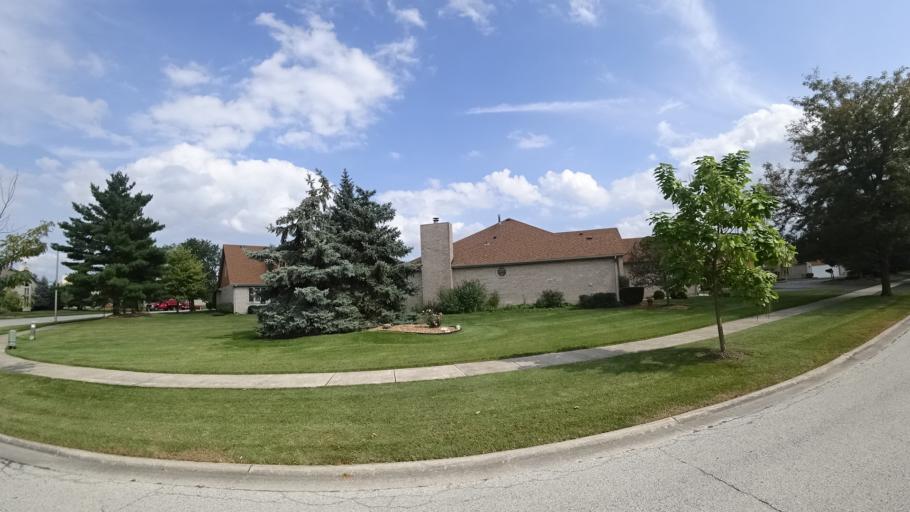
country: US
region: Illinois
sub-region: Cook County
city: Tinley Park
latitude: 41.5576
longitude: -87.7775
